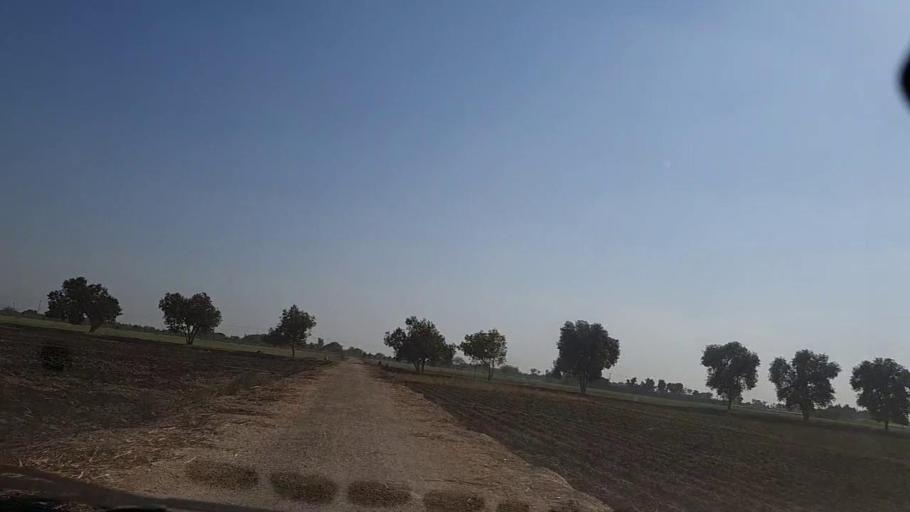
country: PK
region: Sindh
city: Mirpur Khas
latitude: 25.5078
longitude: 68.9095
